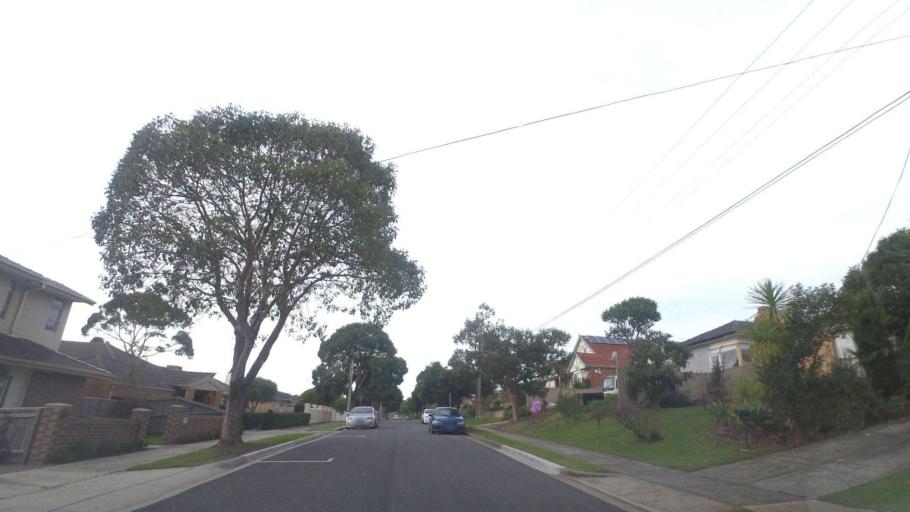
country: AU
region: Victoria
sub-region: Manningham
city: Bulleen
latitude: -37.7747
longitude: 145.0901
